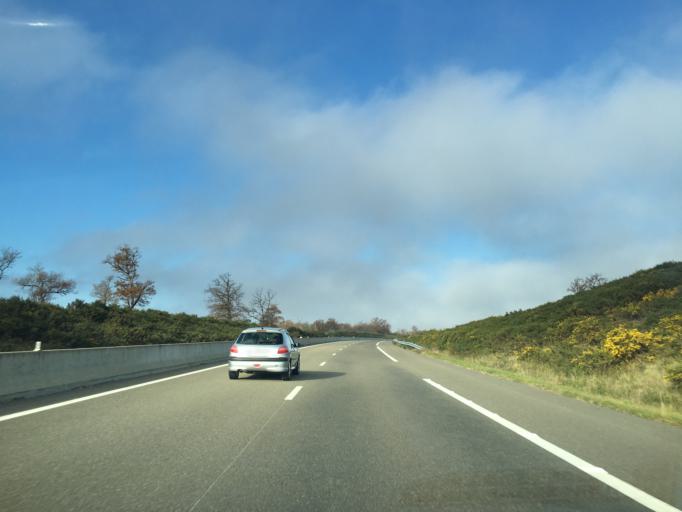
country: FR
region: Aquitaine
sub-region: Departement des Landes
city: Villeneuve-de-Marsan
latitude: 43.7995
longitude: -0.2991
